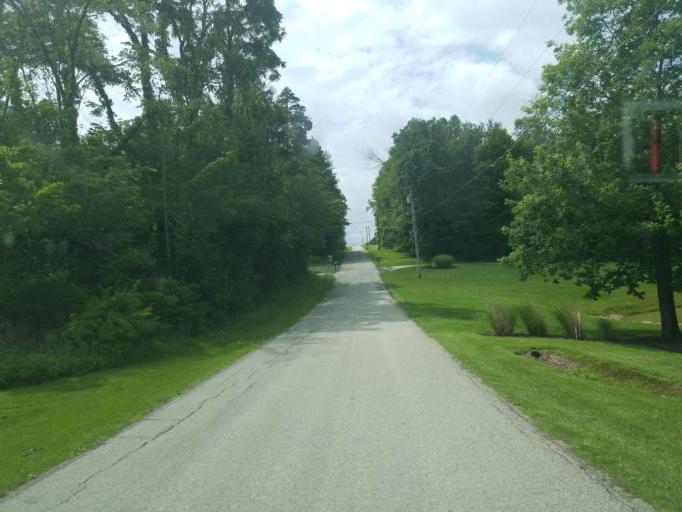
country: US
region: Ohio
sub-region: Richland County
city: Ontario
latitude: 40.7271
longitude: -82.6269
